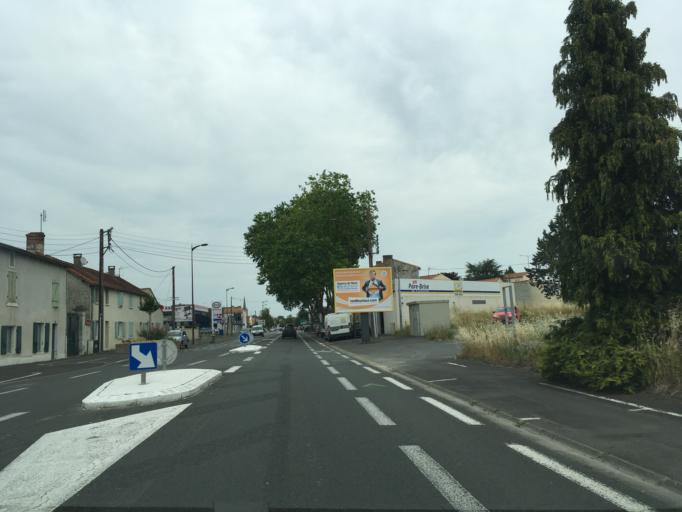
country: FR
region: Poitou-Charentes
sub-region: Departement des Deux-Sevres
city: Niort
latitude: 46.3125
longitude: -0.4782
